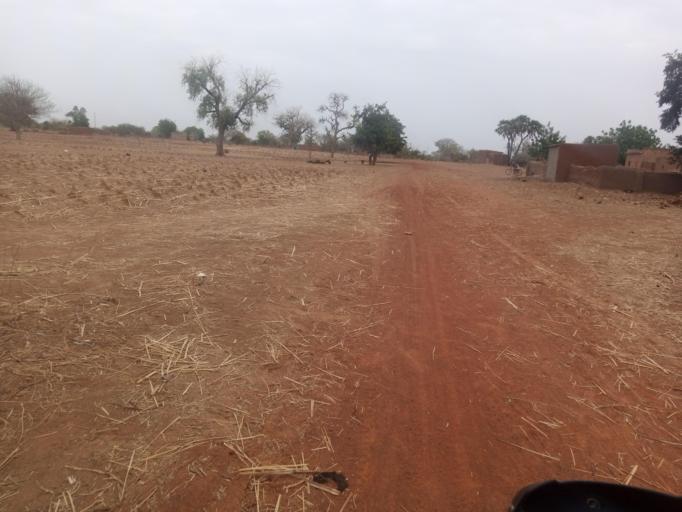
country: BF
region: Boucle du Mouhoun
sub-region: Province de la Kossi
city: Nouna
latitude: 12.8548
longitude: -4.0736
